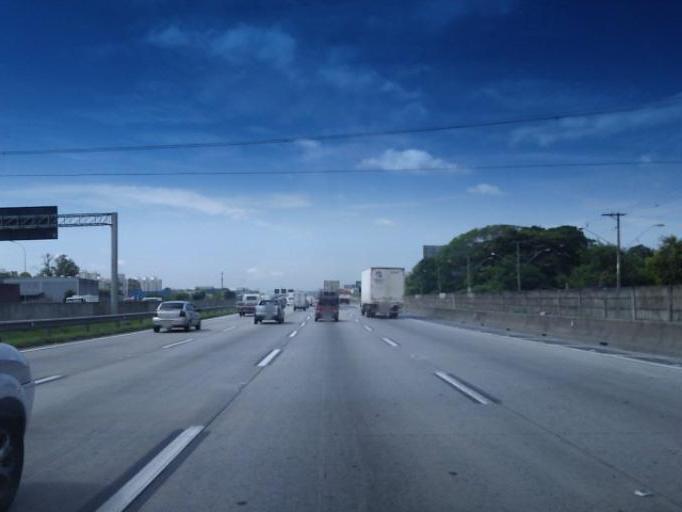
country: BR
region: Sao Paulo
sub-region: Carapicuiba
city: Carapicuiba
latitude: -23.5274
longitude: -46.8174
